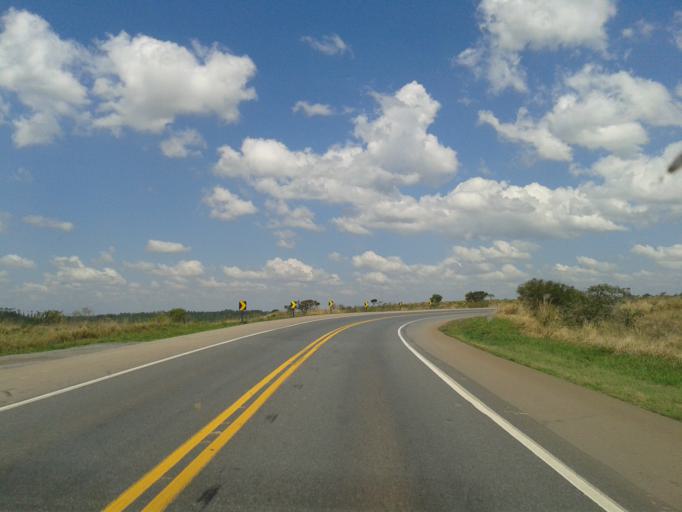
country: BR
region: Minas Gerais
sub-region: Campos Altos
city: Campos Altos
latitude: -19.6835
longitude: -46.0399
